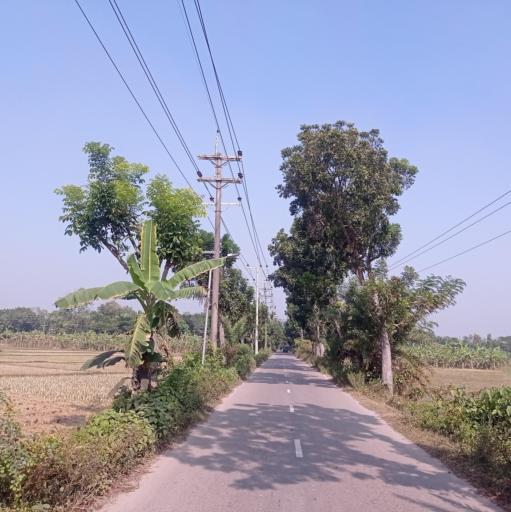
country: BD
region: Dhaka
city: Narsingdi
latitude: 24.0356
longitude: 90.6756
